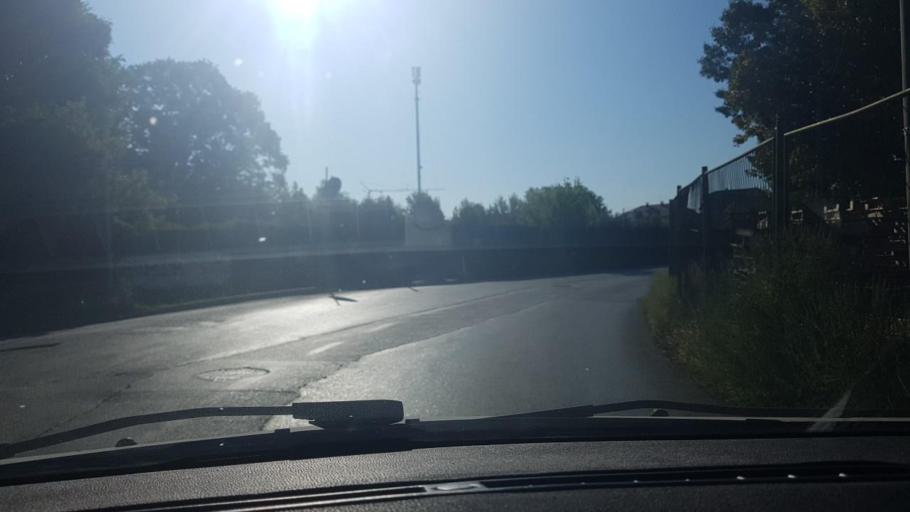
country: HR
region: Grad Zagreb
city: Novi Zagreb
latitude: 45.7672
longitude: 15.9585
